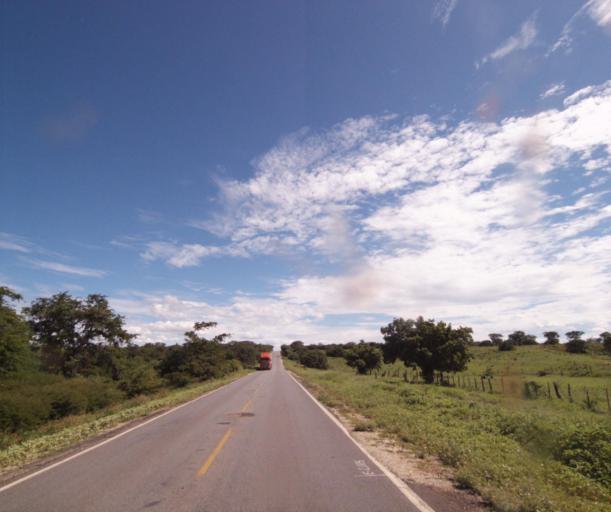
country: BR
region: Bahia
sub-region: Guanambi
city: Guanambi
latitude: -14.5652
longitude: -42.7028
